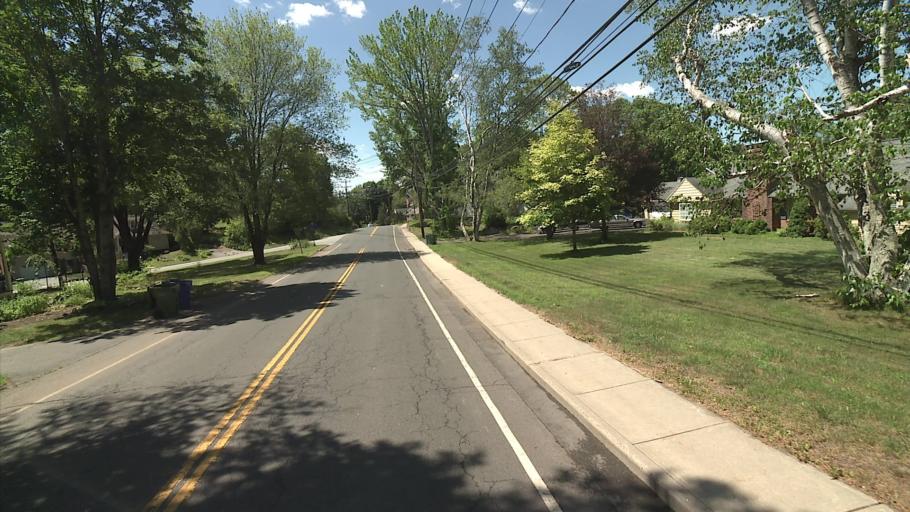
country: US
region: Connecticut
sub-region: Middlesex County
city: East Hampton
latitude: 41.5805
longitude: -72.4969
